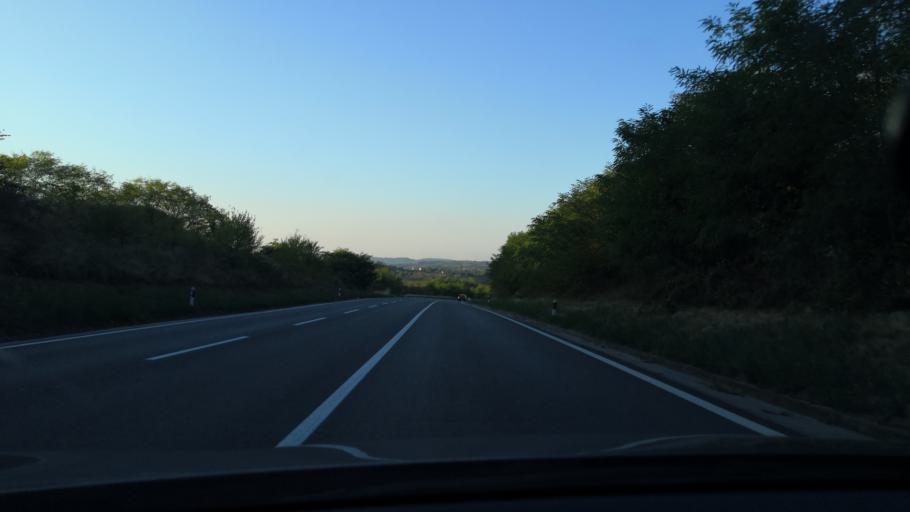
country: RS
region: Central Serbia
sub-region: Belgrade
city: Sopot
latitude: 44.5428
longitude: 20.6588
